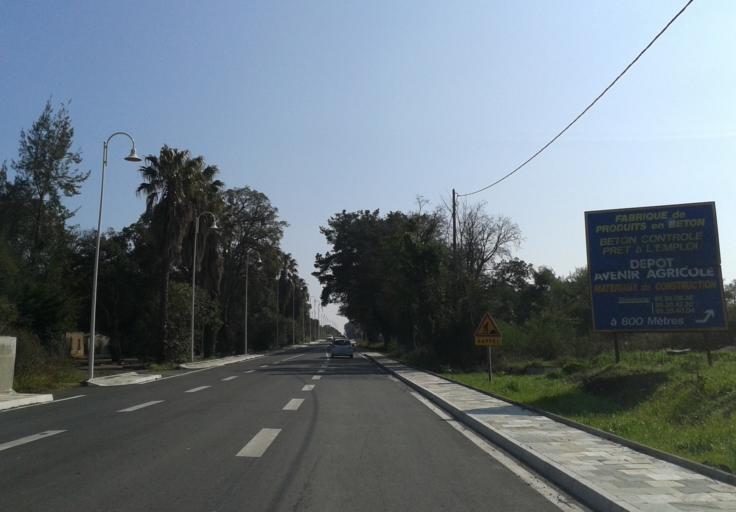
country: FR
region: Corsica
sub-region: Departement de la Haute-Corse
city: San-Nicolao
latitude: 42.3556
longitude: 9.5312
